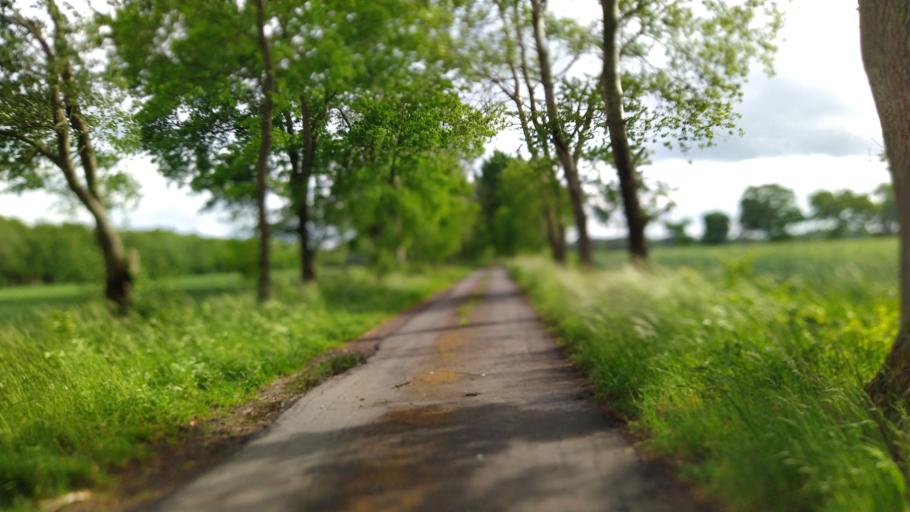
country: DE
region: Lower Saxony
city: Farven
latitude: 53.4271
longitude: 9.3536
